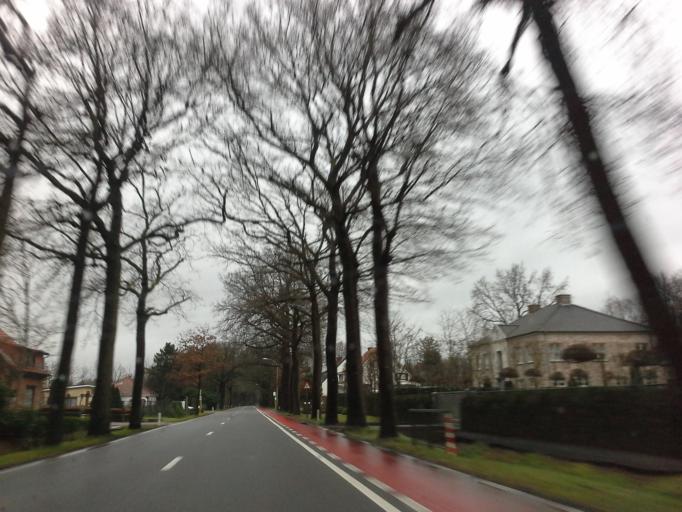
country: BE
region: Flanders
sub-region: Provincie Antwerpen
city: Baarle-Hertog
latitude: 51.3758
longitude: 4.9359
